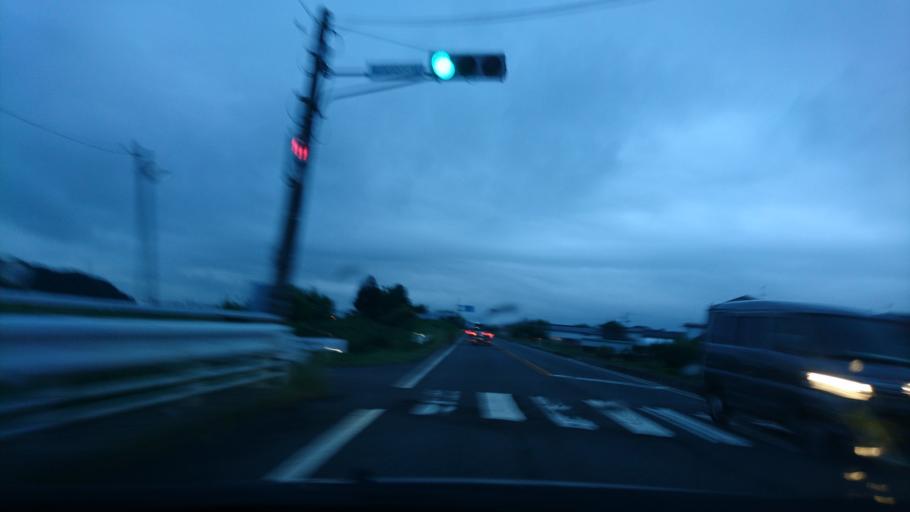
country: JP
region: Iwate
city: Ichinoseki
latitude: 38.8152
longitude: 141.0770
